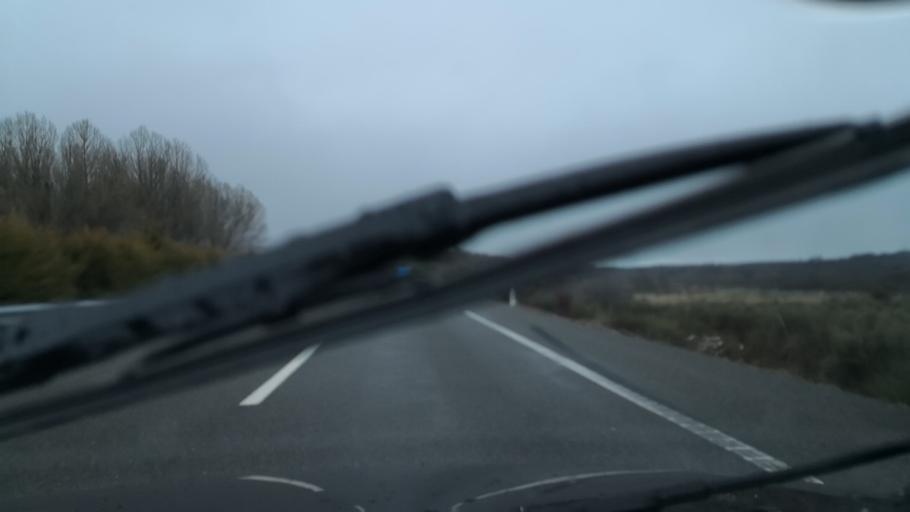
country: ES
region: Castille and Leon
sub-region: Provincia de Zamora
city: Cobreros
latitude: 42.0492
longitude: -6.6903
